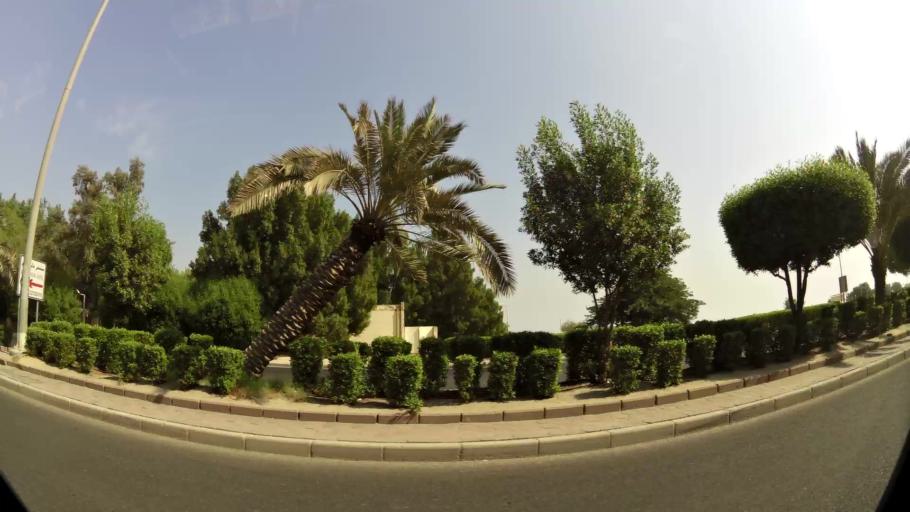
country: KW
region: Al Ahmadi
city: Al Mahbulah
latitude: 29.1463
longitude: 48.1281
